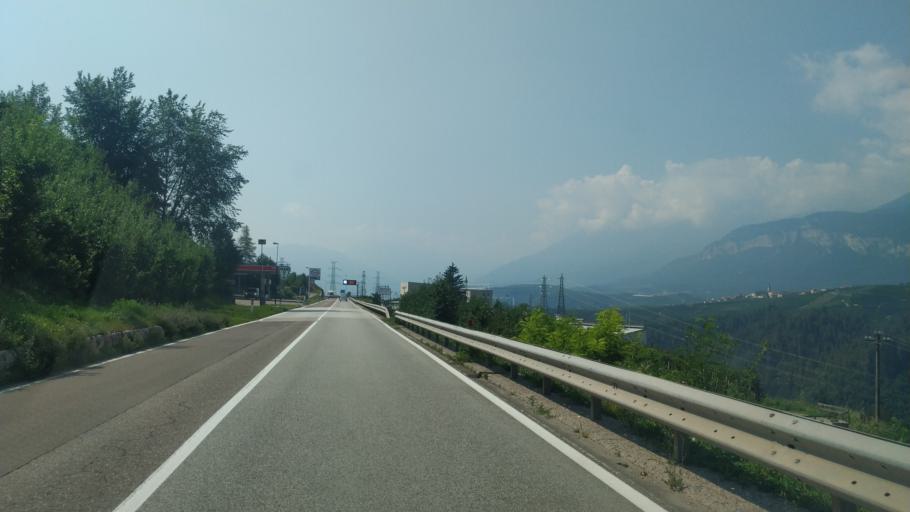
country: IT
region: Trentino-Alto Adige
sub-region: Provincia di Trento
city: Taio
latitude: 46.3306
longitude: 11.0640
